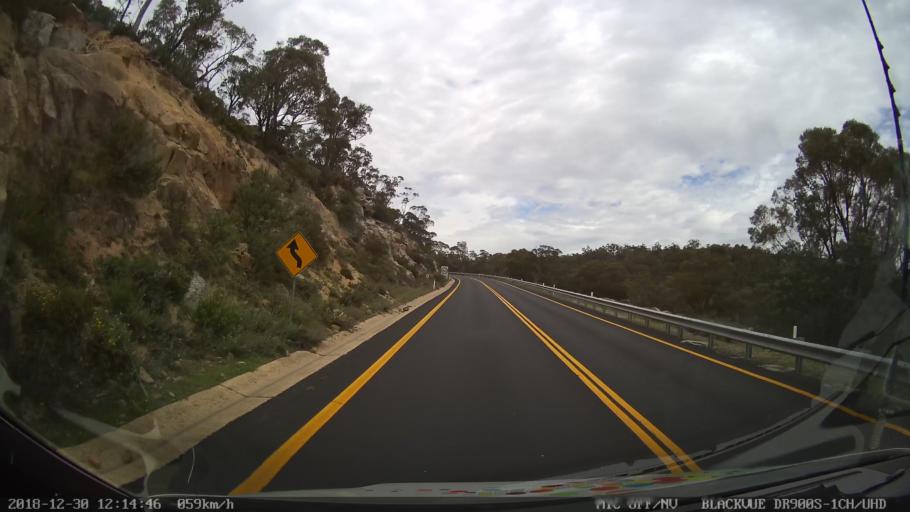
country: AU
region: New South Wales
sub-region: Snowy River
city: Jindabyne
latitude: -36.3423
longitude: 148.5777
